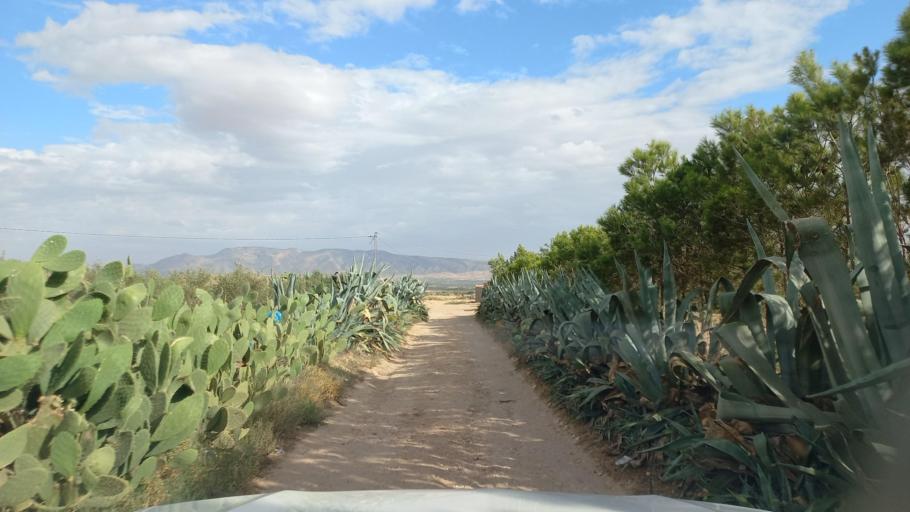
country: TN
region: Al Qasrayn
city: Sbiba
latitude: 35.4493
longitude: 9.0852
